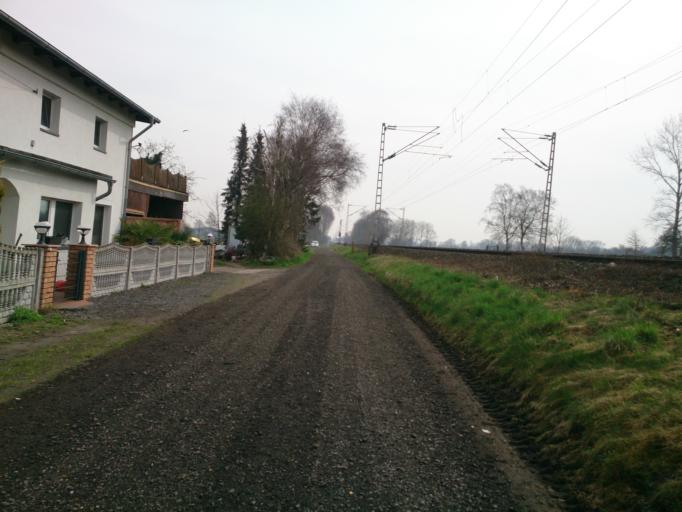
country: DE
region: Lower Saxony
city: Buxtehude
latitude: 53.4699
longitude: 9.7310
